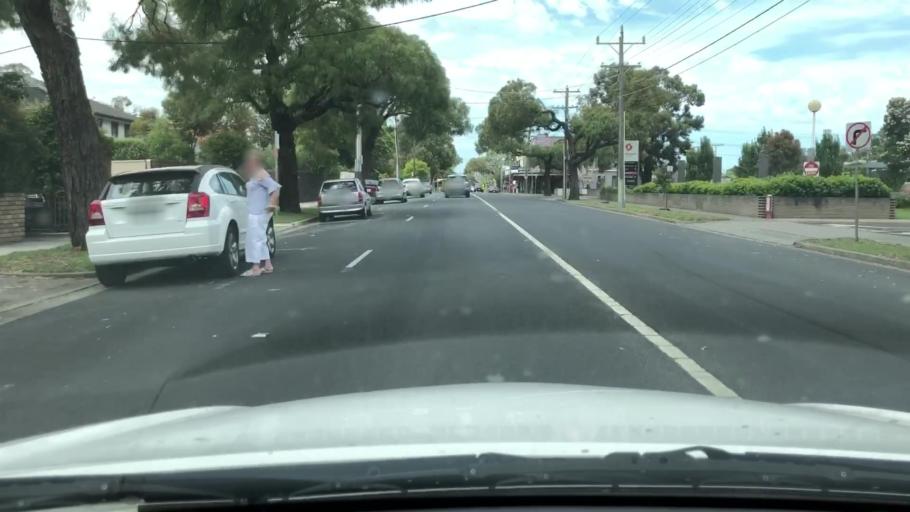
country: AU
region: Victoria
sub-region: Bayside
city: Black Rock
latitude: -37.9608
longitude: 145.0192
